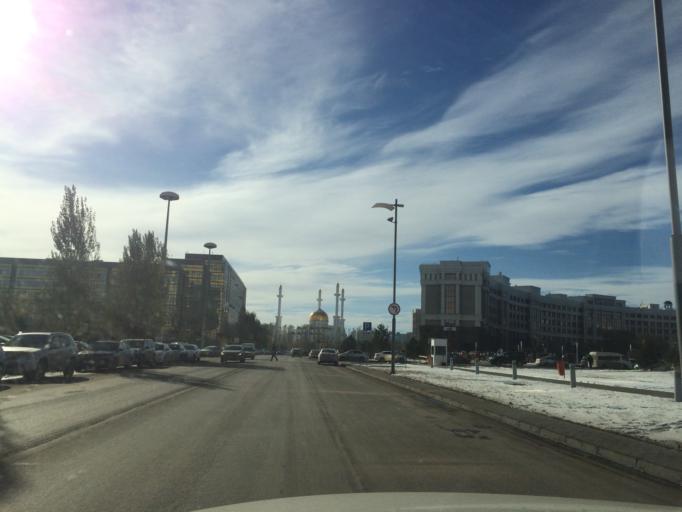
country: KZ
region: Astana Qalasy
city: Astana
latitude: 51.1314
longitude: 71.4177
